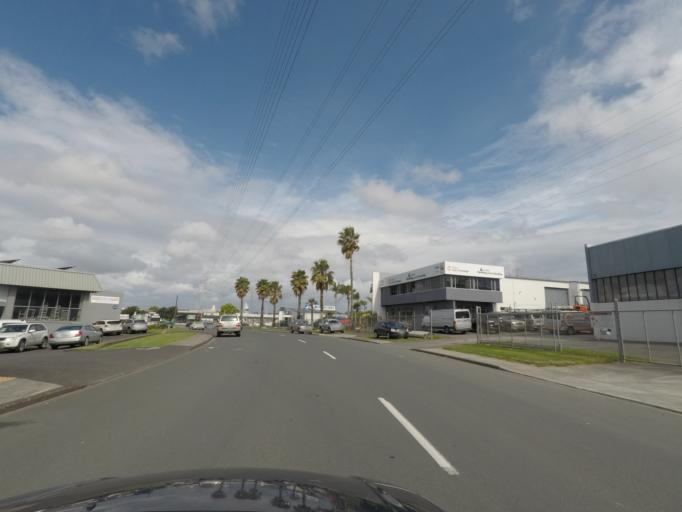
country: NZ
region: Auckland
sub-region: Auckland
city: Rosebank
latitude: -36.8483
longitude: 174.6337
